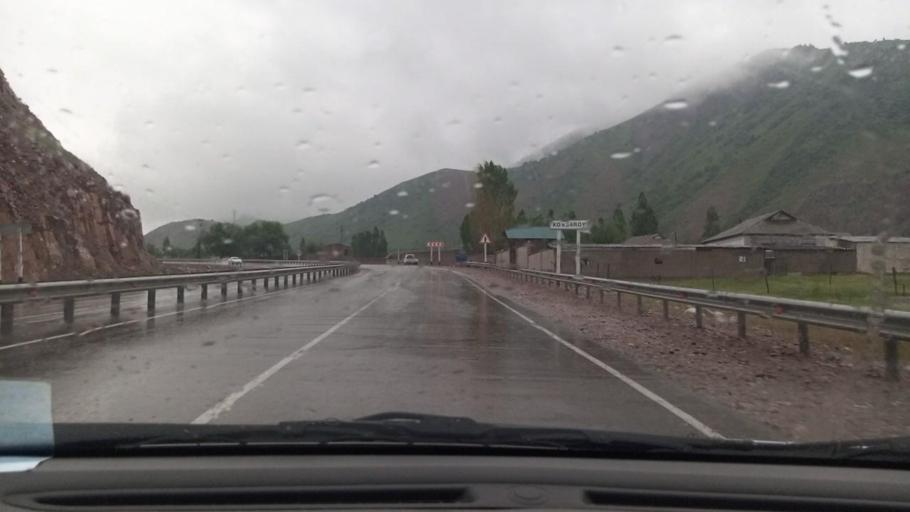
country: UZ
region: Toshkent
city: Angren
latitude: 41.1039
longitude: 70.3326
